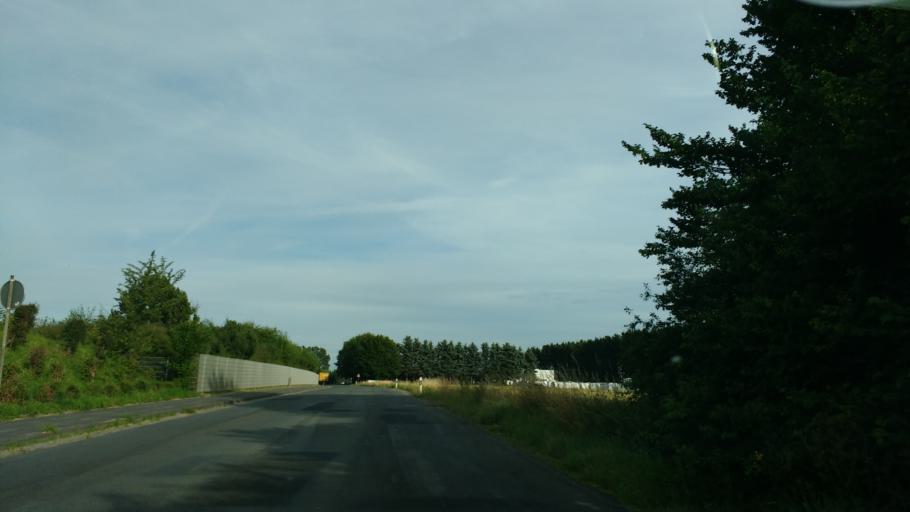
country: DE
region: North Rhine-Westphalia
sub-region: Regierungsbezirk Detmold
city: Horn
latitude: 51.8822
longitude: 8.9425
